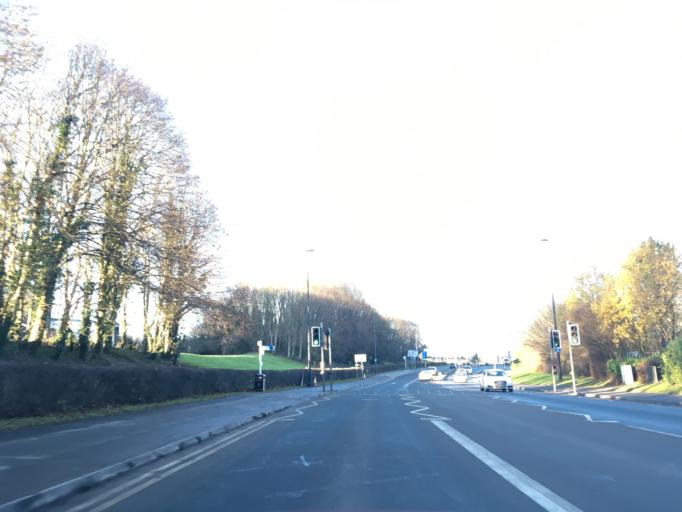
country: GB
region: England
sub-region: South Gloucestershire
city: Stoke Gifford
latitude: 51.5022
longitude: -2.5447
